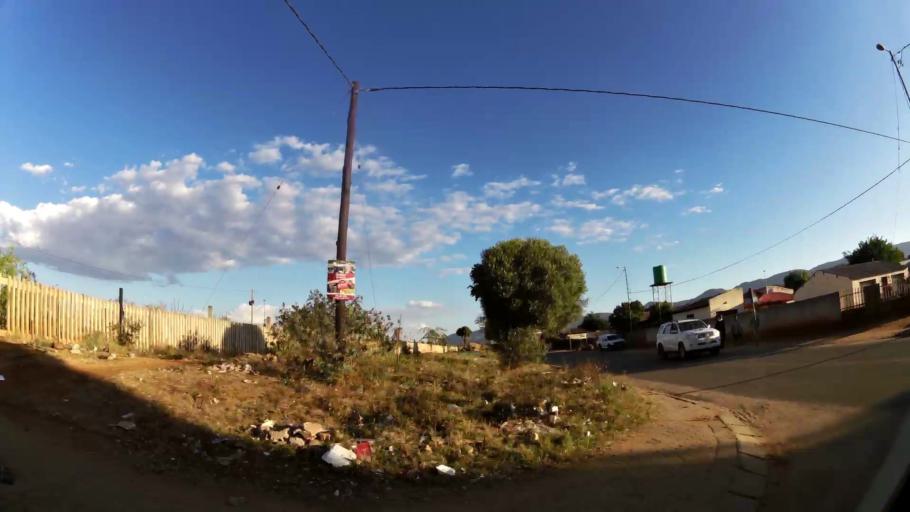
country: ZA
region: Limpopo
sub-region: Waterberg District Municipality
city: Mokopane
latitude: -24.1495
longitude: 28.9873
